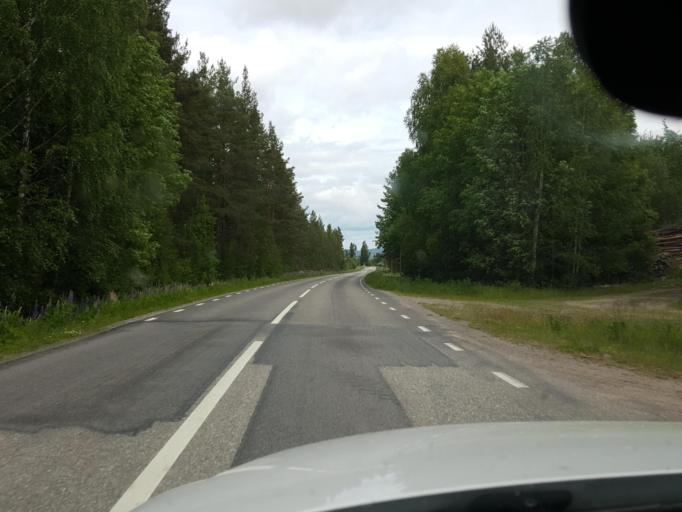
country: SE
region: Gaevleborg
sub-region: Ljusdals Kommun
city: Farila
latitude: 61.8005
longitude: 15.7146
